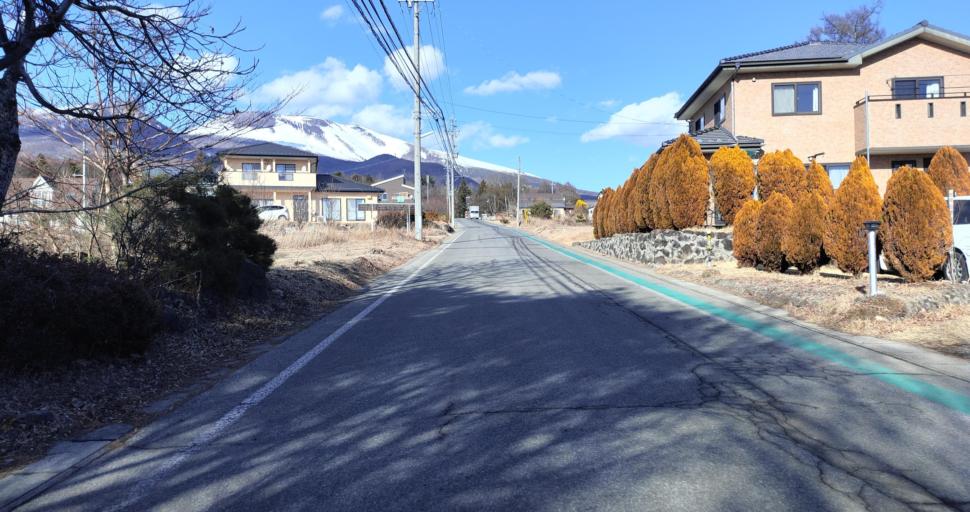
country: JP
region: Nagano
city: Komoro
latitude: 36.3334
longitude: 138.5121
